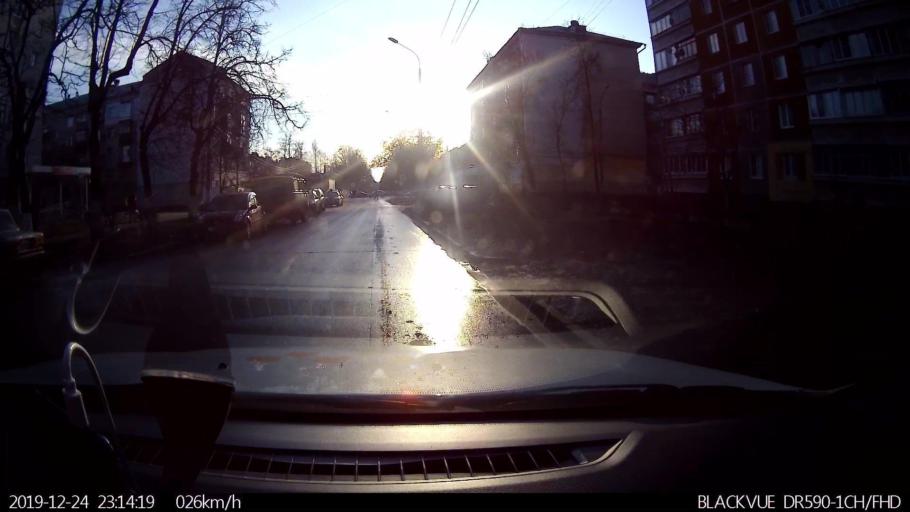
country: RU
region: Nizjnij Novgorod
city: Gorbatovka
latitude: 56.2501
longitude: 43.8581
